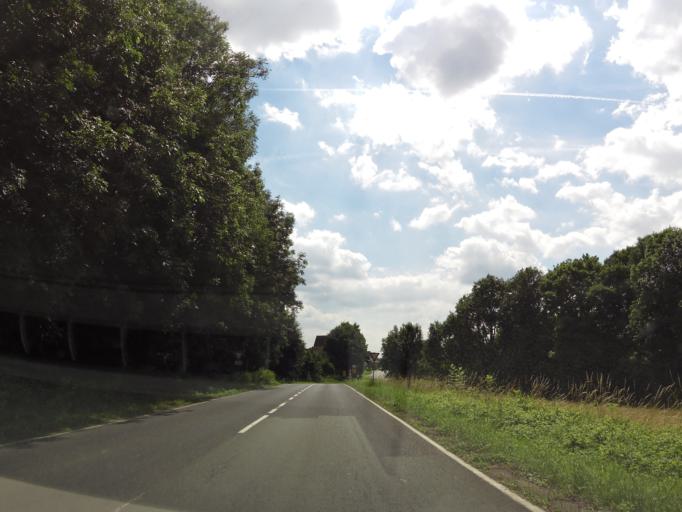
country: DE
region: Lower Saxony
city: Boffzen
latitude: 51.7614
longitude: 9.4076
